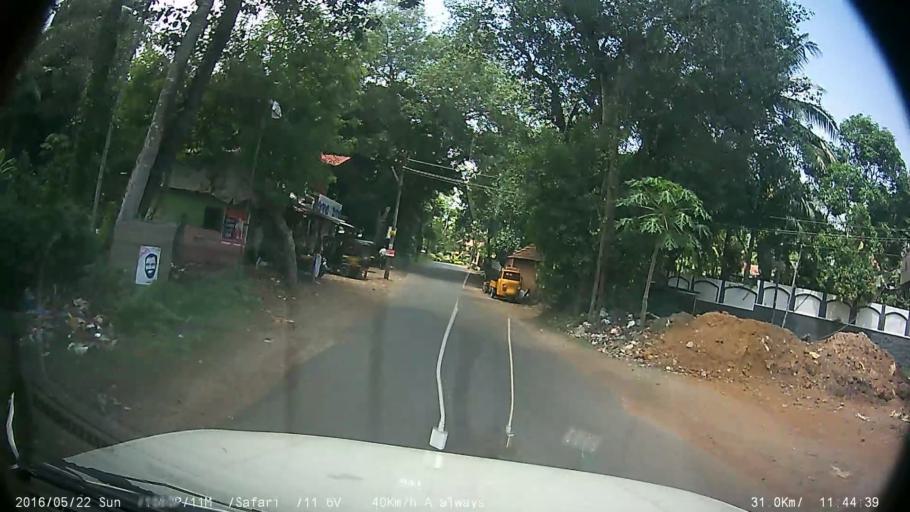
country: IN
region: Kerala
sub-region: Kottayam
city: Kottayam
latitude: 9.5439
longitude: 76.5191
